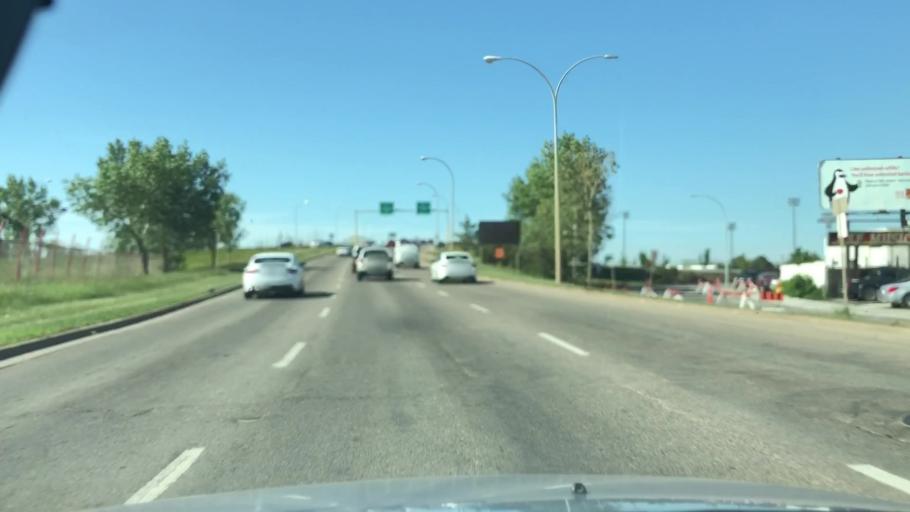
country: CA
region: Alberta
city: Edmonton
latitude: 53.5727
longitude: -113.4522
